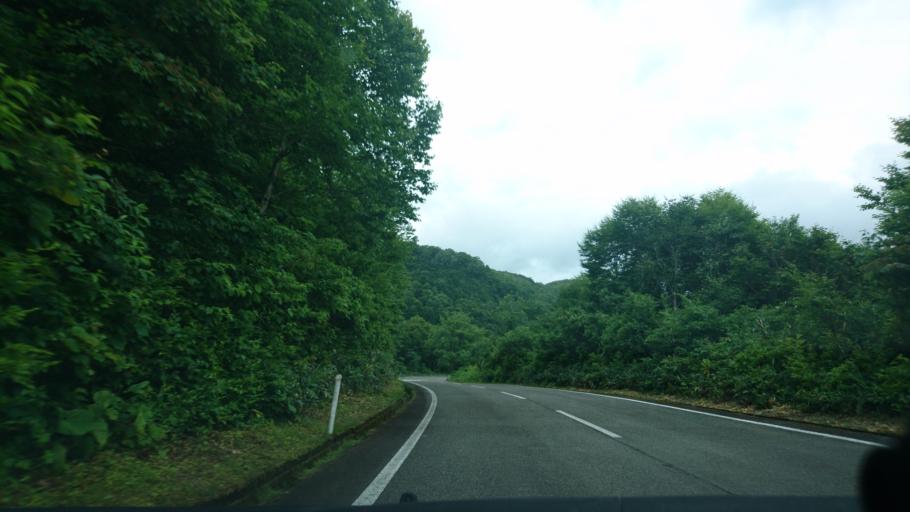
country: JP
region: Akita
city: Yuzawa
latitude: 39.1549
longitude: 140.7527
